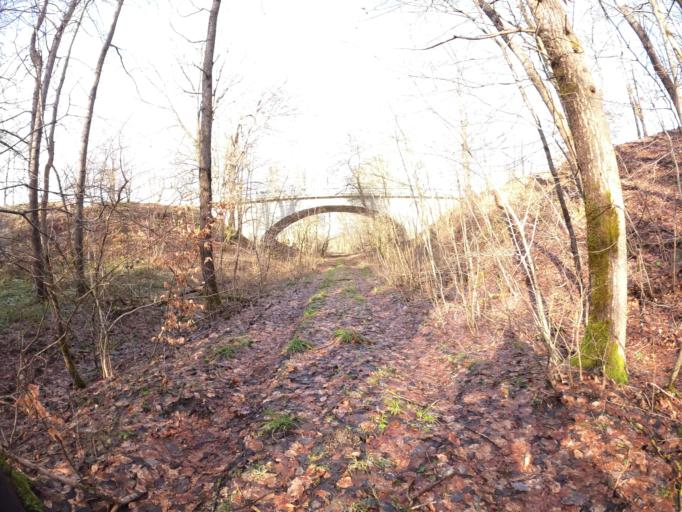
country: PL
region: West Pomeranian Voivodeship
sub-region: Powiat koszalinski
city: Polanow
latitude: 54.1410
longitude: 16.7703
